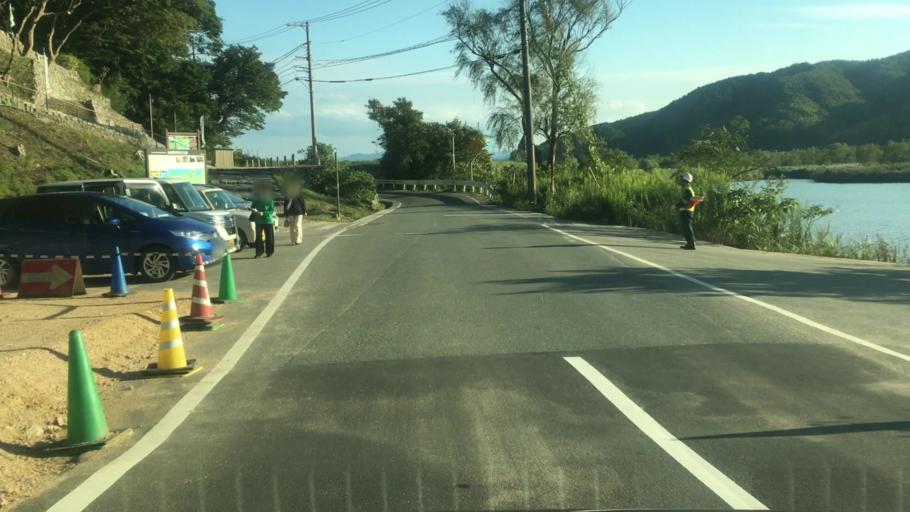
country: JP
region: Hyogo
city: Toyooka
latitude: 35.5886
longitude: 134.8038
